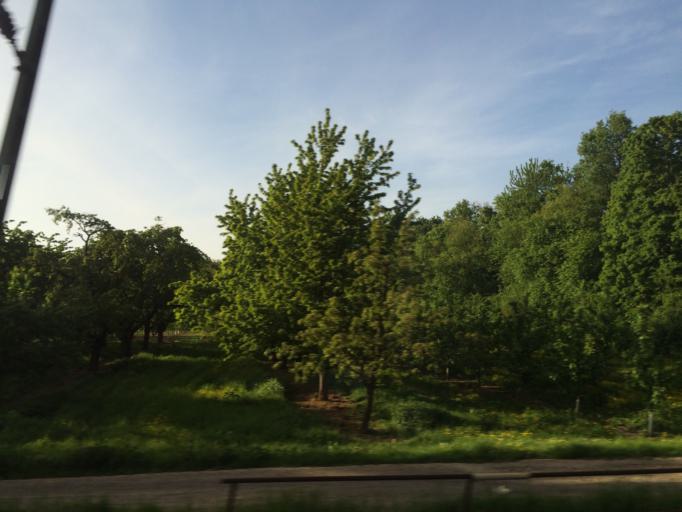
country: DE
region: Hesse
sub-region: Regierungsbezirk Darmstadt
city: Walluf
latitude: 50.0483
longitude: 8.1736
